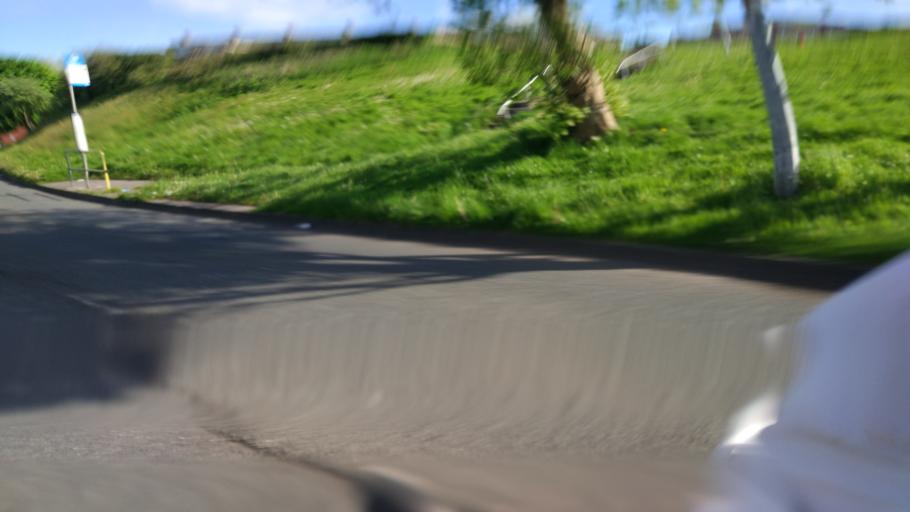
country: IE
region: Munster
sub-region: County Cork
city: Cork
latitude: 51.9113
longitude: -8.4591
